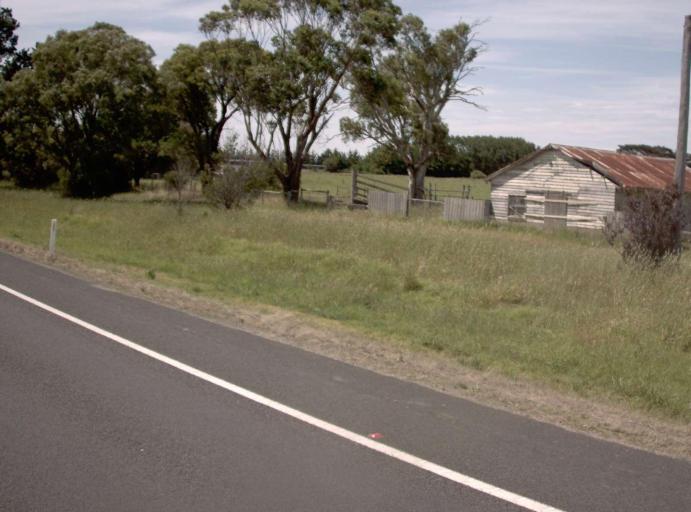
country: AU
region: Victoria
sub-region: Wellington
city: Sale
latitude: -38.0550
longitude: 147.0680
